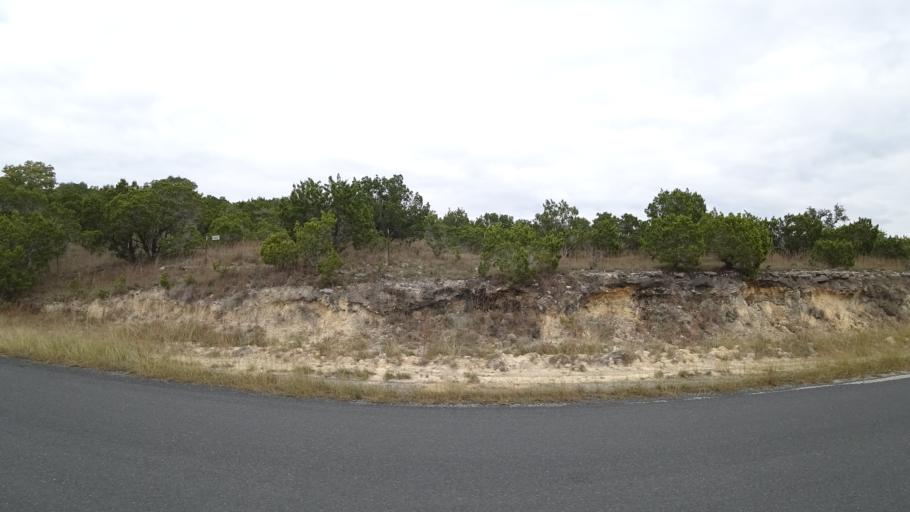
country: US
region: Texas
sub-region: Travis County
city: Bee Cave
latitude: 30.3515
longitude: -97.9294
